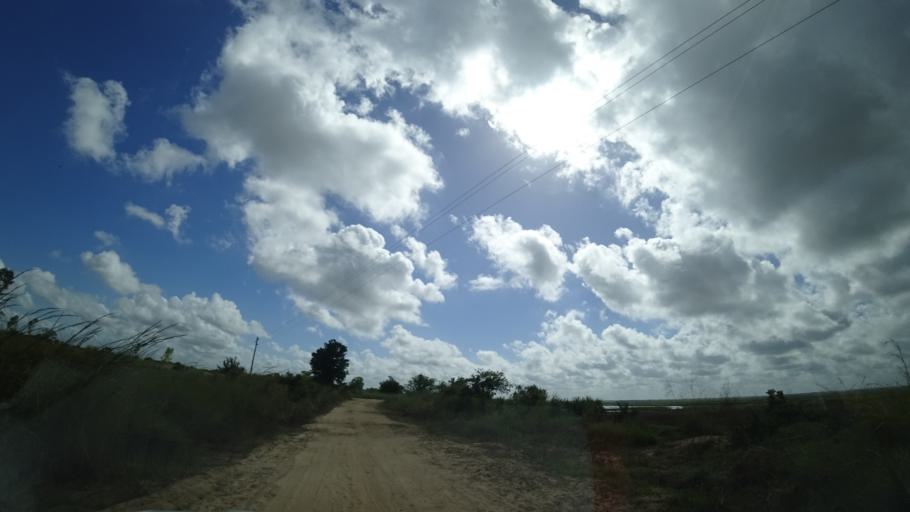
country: MZ
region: Sofala
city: Dondo
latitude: -19.4291
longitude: 34.5607
